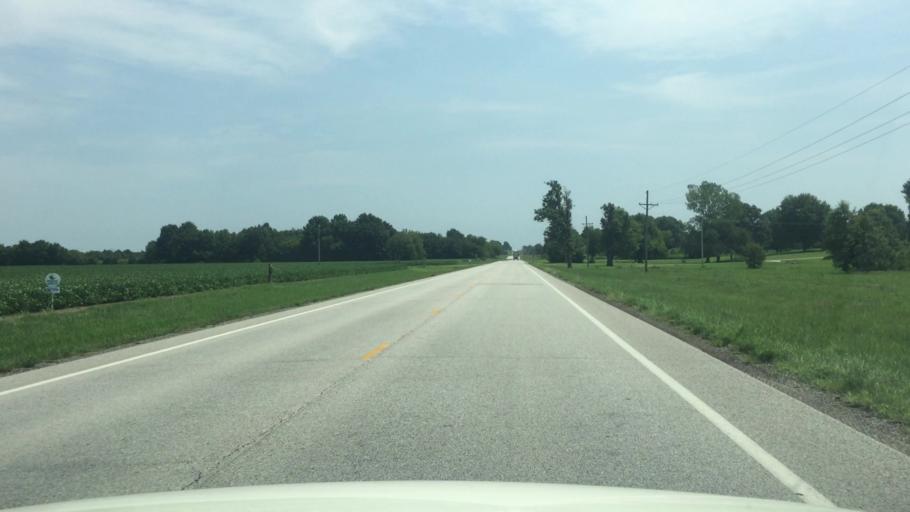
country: US
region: Kansas
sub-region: Cherokee County
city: Columbus
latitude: 37.1781
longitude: -94.8114
